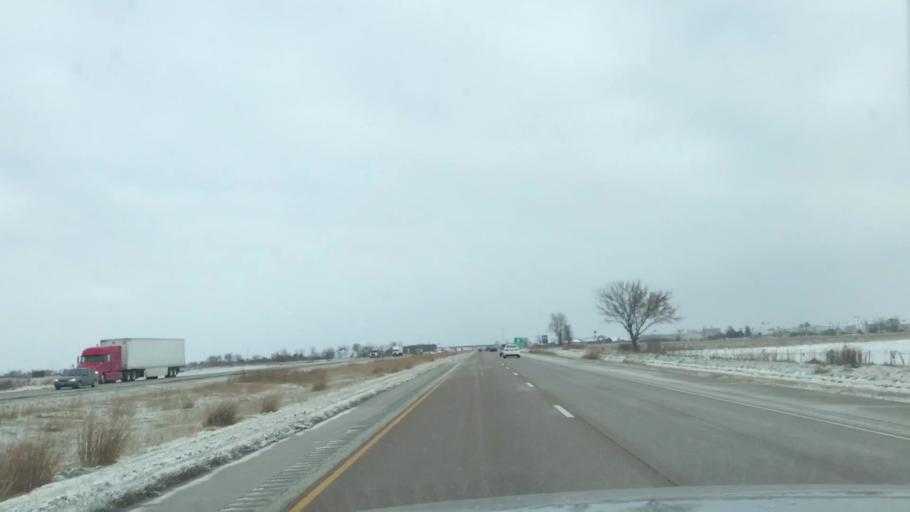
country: US
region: Illinois
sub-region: Montgomery County
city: Litchfield
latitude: 39.1624
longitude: -89.6895
